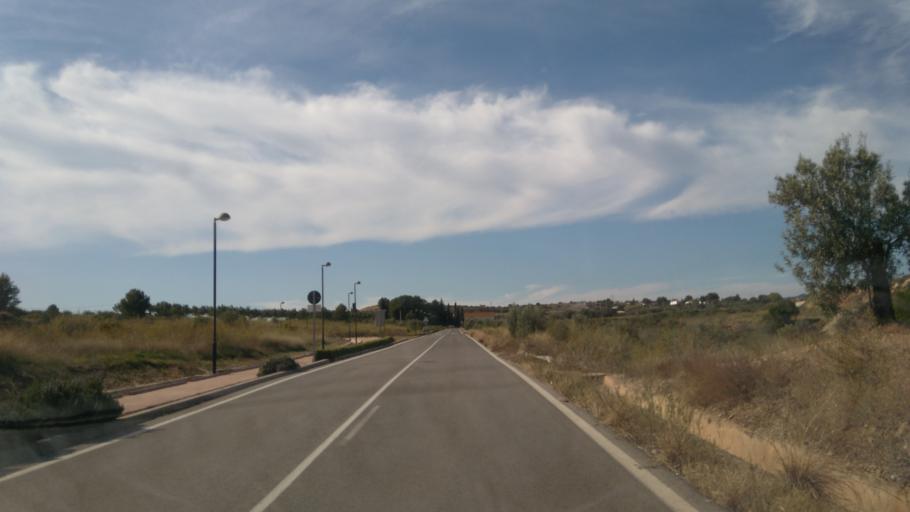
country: ES
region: Valencia
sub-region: Provincia de Valencia
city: Montroy
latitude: 39.3431
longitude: -0.6174
